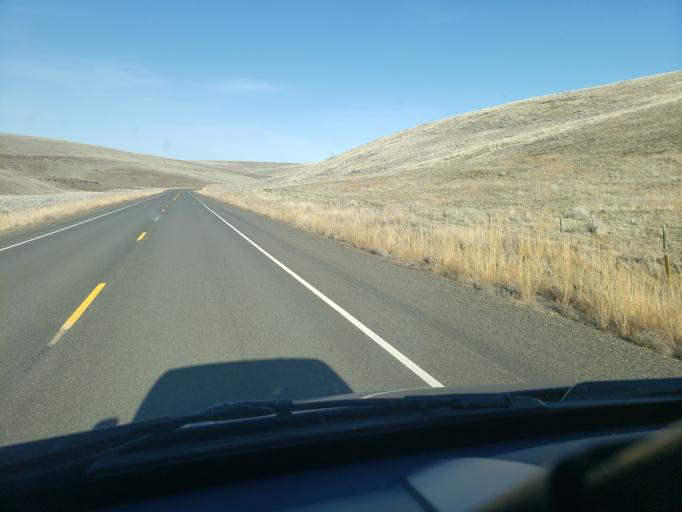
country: US
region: Oregon
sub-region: Umatilla County
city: Pilot Rock
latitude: 45.4632
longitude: -118.9271
